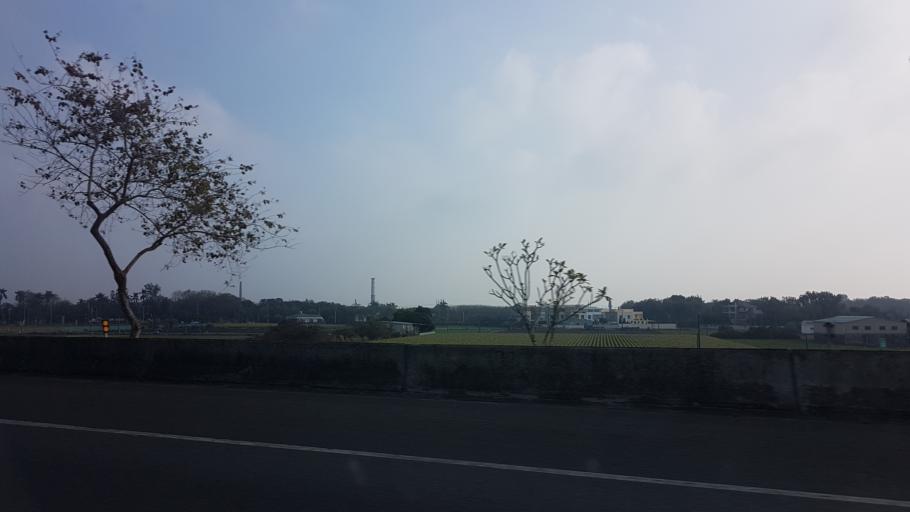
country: TW
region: Taiwan
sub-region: Chiayi
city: Taibao
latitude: 23.4200
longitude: 120.3782
